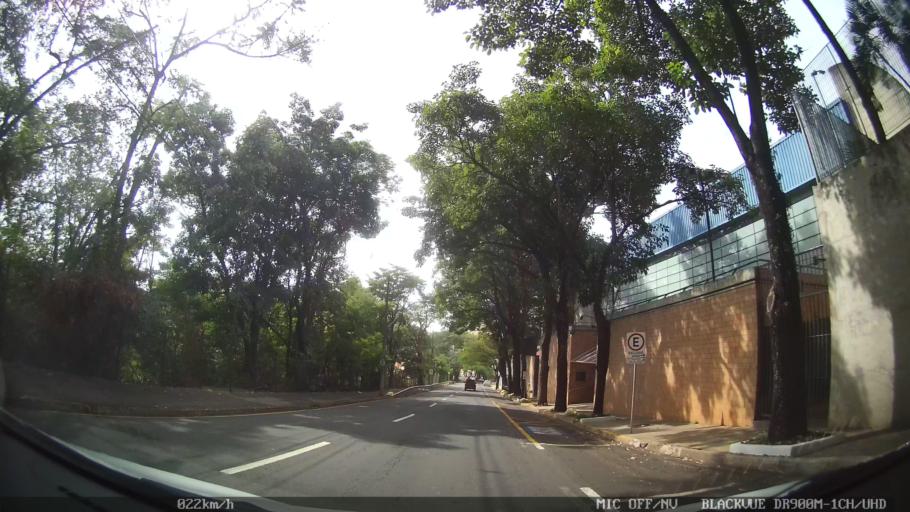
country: BR
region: Sao Paulo
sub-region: Piracicaba
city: Piracicaba
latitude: -22.7258
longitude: -47.6565
